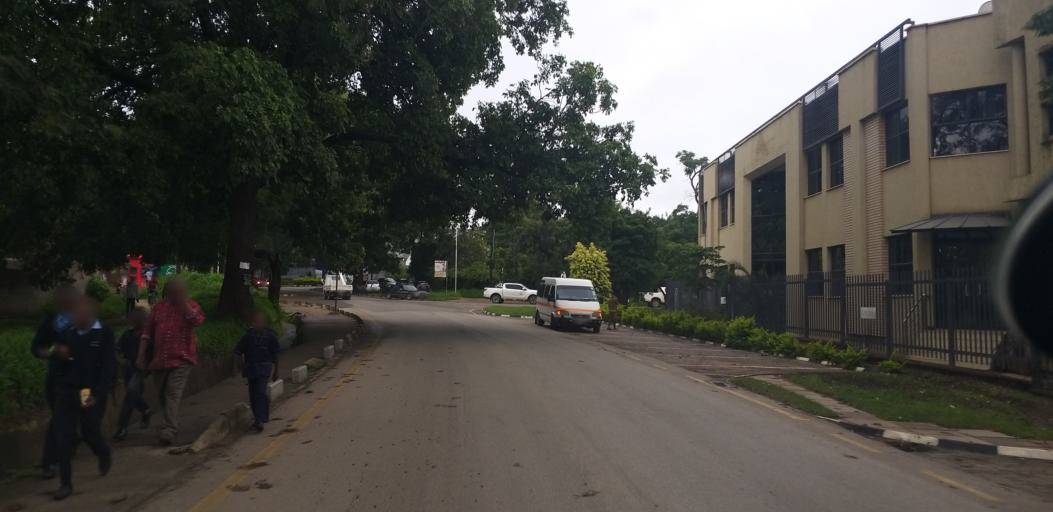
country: ZM
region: Lusaka
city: Lusaka
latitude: -15.4197
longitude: 28.2990
